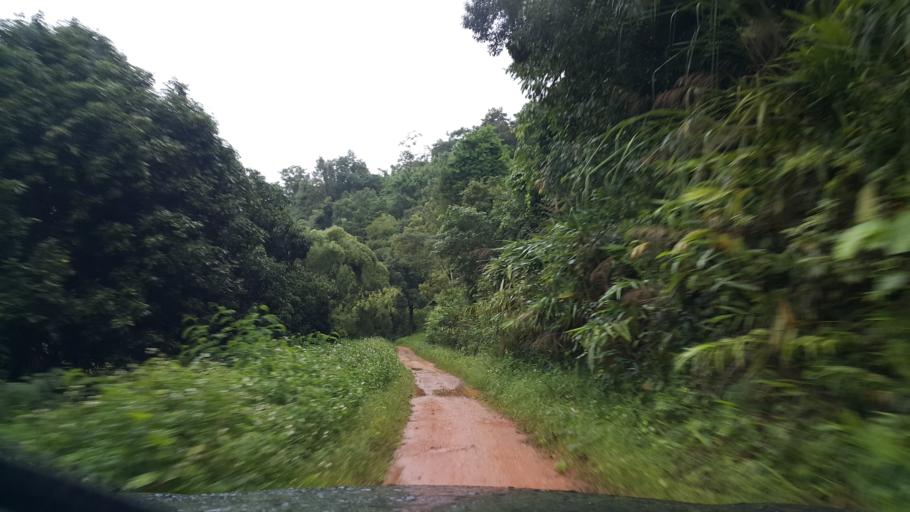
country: TH
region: Phayao
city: Phu Sang
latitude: 19.6244
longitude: 100.4133
